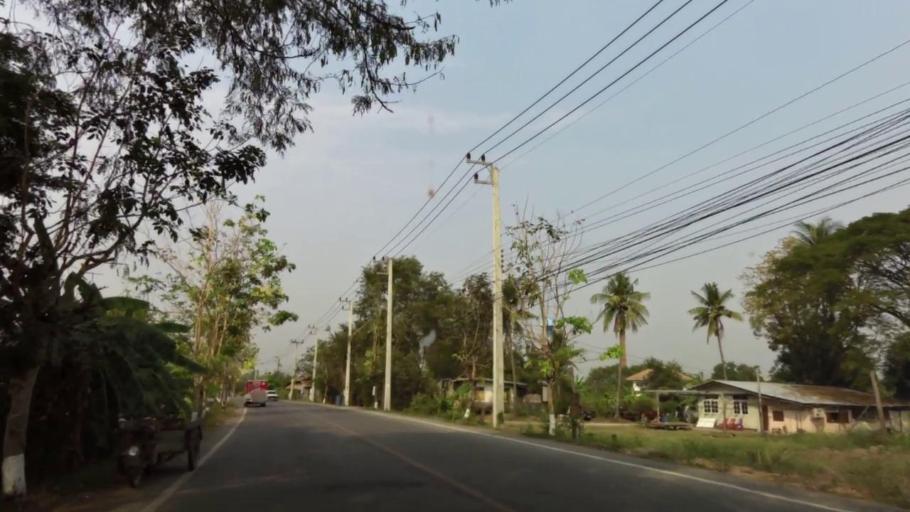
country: TH
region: Phra Nakhon Si Ayutthaya
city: Phra Nakhon Si Ayutthaya
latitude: 14.3395
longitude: 100.5745
